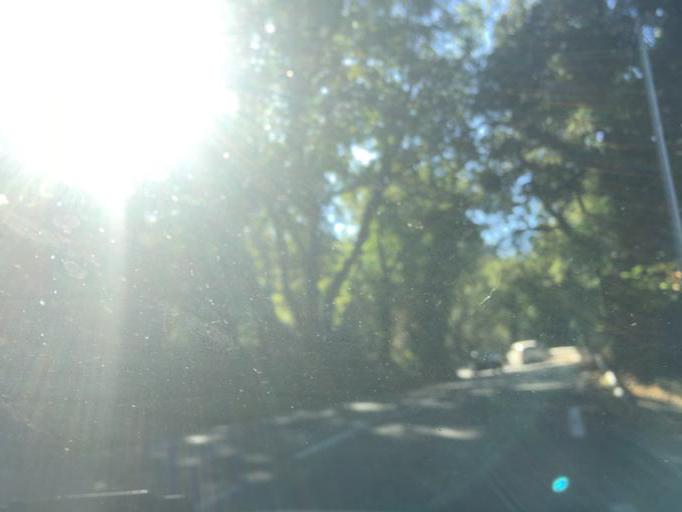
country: FR
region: Provence-Alpes-Cote d'Azur
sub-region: Departement du Var
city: La Garde-Freinet
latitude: 43.3239
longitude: 6.4755
